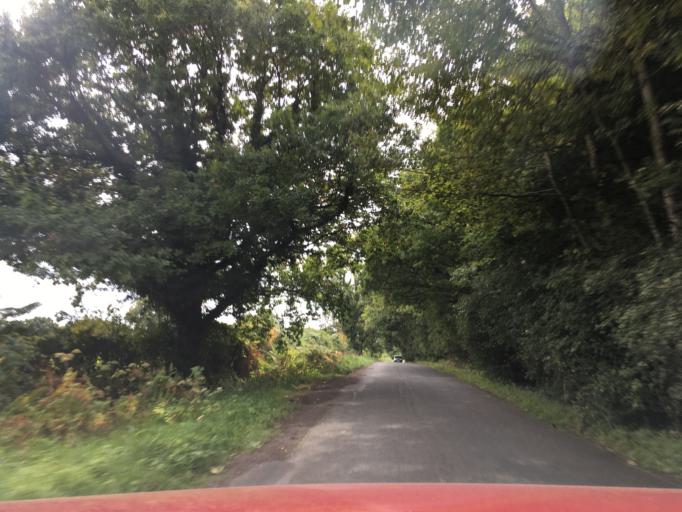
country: GB
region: England
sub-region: South Gloucestershire
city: Charfield
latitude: 51.6520
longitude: -2.4220
